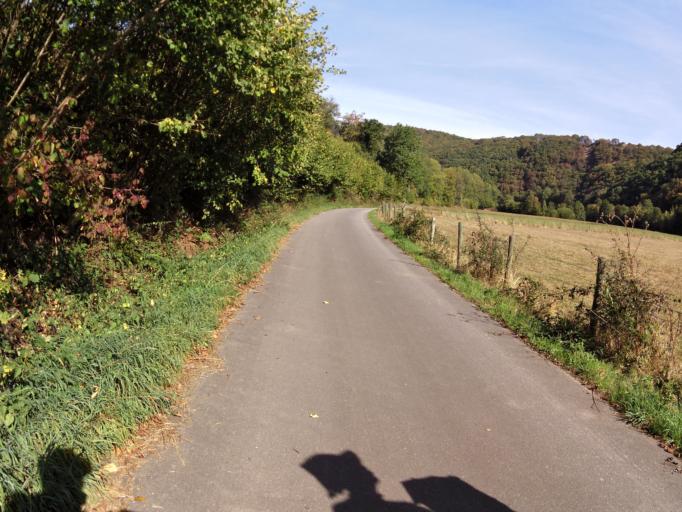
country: DE
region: Rheinland-Pfalz
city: Niederraden
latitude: 49.9830
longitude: 6.3124
